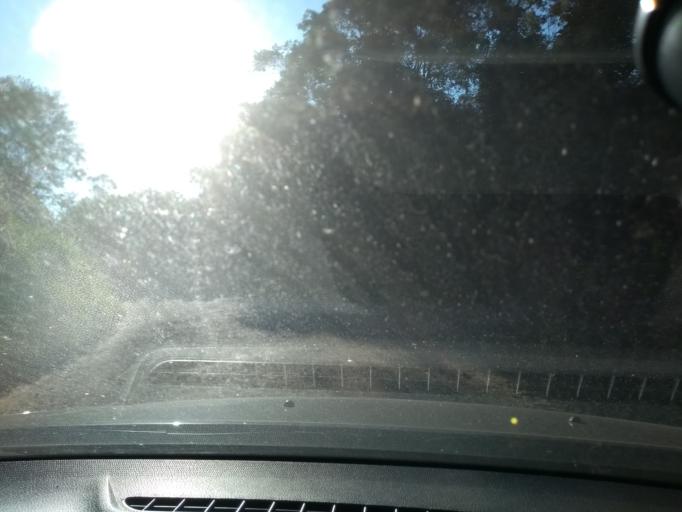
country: BR
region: Sao Paulo
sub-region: Rio Grande Da Serra
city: Rio Grande da Serra
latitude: -23.7777
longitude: -46.4920
